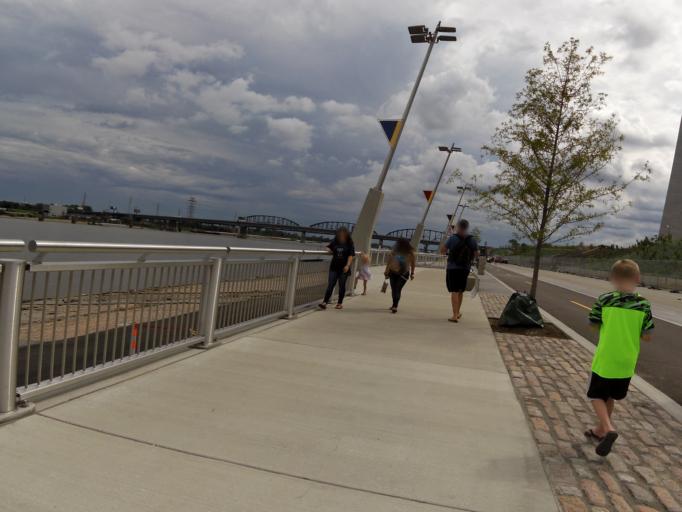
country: US
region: Missouri
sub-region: City of Saint Louis
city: St. Louis
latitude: 38.6258
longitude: -90.1833
